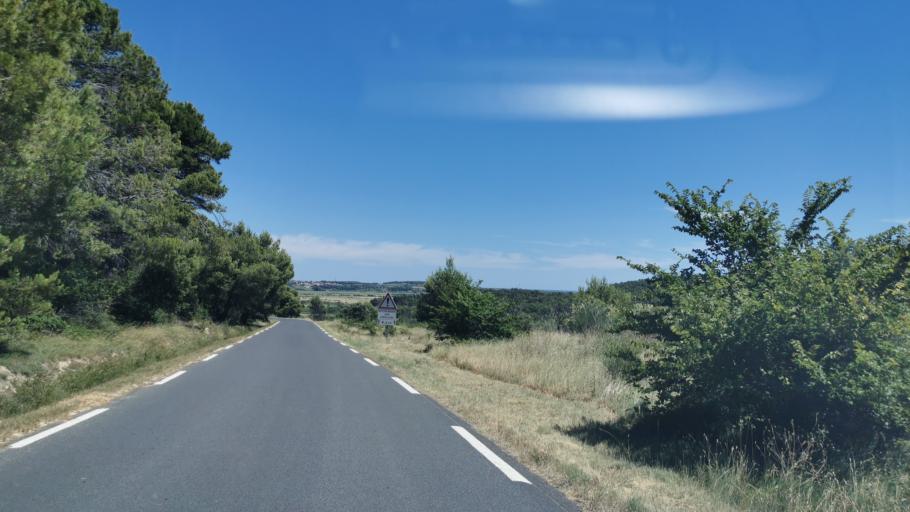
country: FR
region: Languedoc-Roussillon
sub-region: Departement de l'Herault
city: Nissan-lez-Enserune
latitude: 43.2776
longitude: 3.1146
